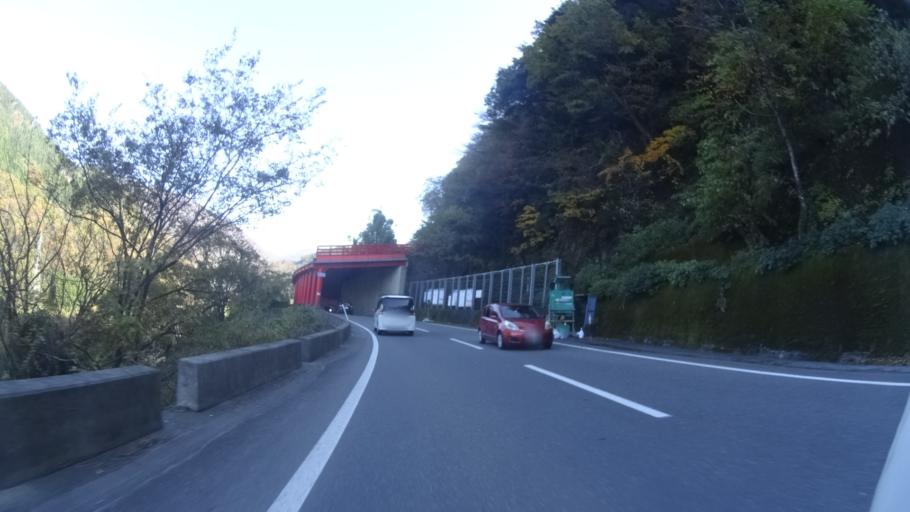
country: JP
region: Fukui
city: Ono
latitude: 35.9674
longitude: 136.5765
